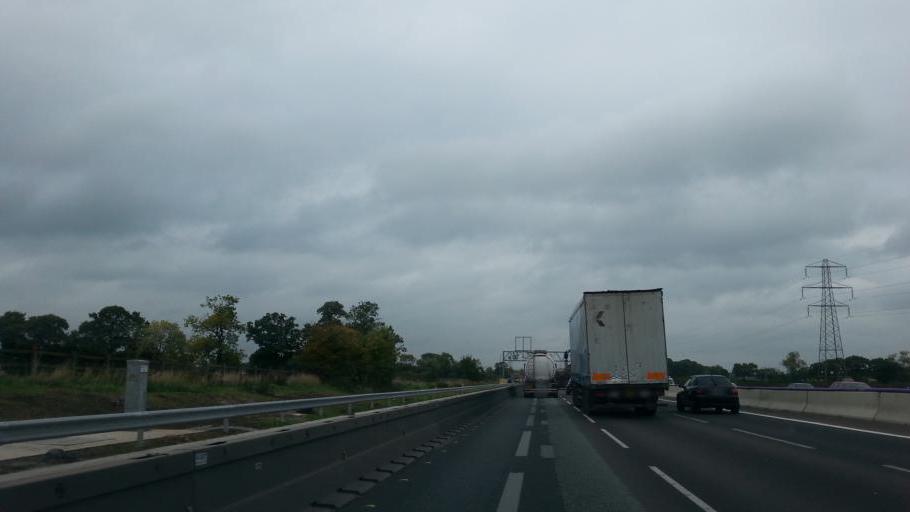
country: GB
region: England
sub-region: Cheshire East
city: Knutsford
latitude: 53.2775
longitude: -2.3973
